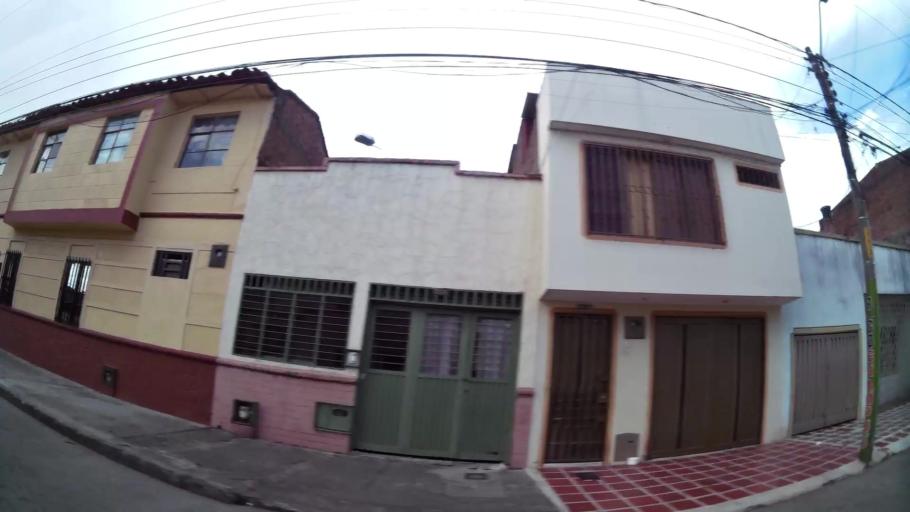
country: CO
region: Valle del Cauca
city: Cali
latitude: 3.4408
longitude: -76.5214
